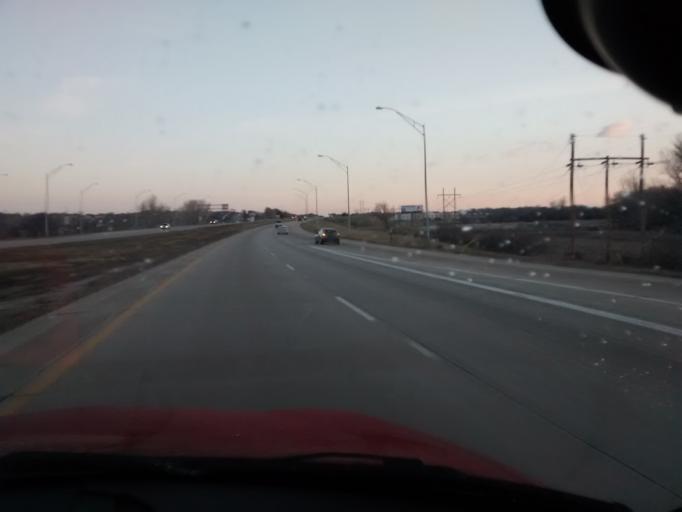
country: US
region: Nebraska
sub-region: Sarpy County
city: Offutt Air Force Base
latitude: 41.1433
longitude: -95.9382
